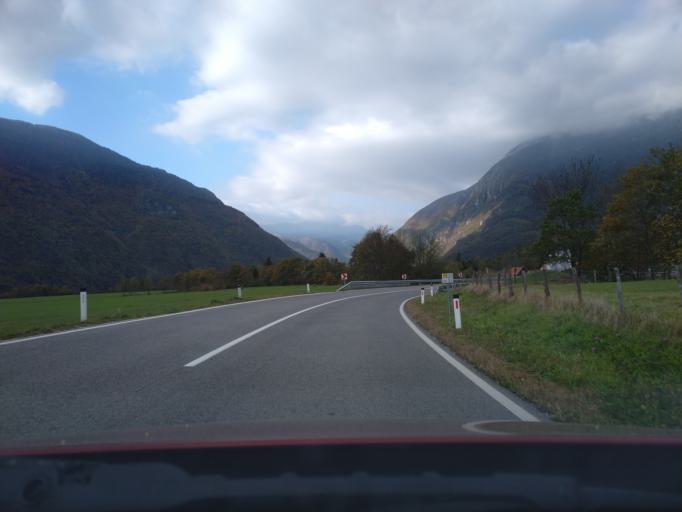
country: SI
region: Bovec
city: Bovec
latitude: 46.3299
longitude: 13.5446
